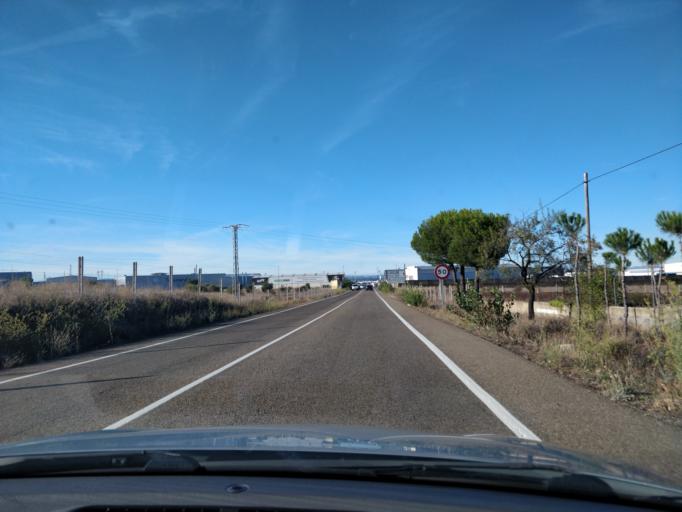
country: ES
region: Castille and Leon
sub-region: Provincia de Leon
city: San Andres del Rabanedo
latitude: 42.5848
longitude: -5.6192
